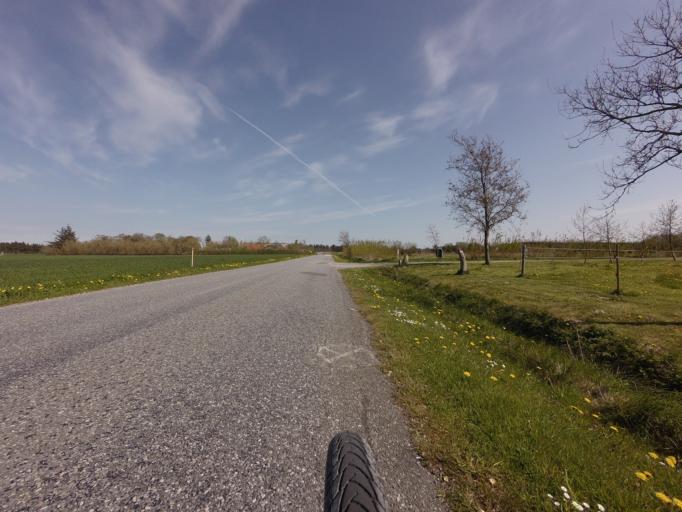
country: DK
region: North Denmark
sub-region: Jammerbugt Kommune
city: Pandrup
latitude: 57.2264
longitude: 9.6372
